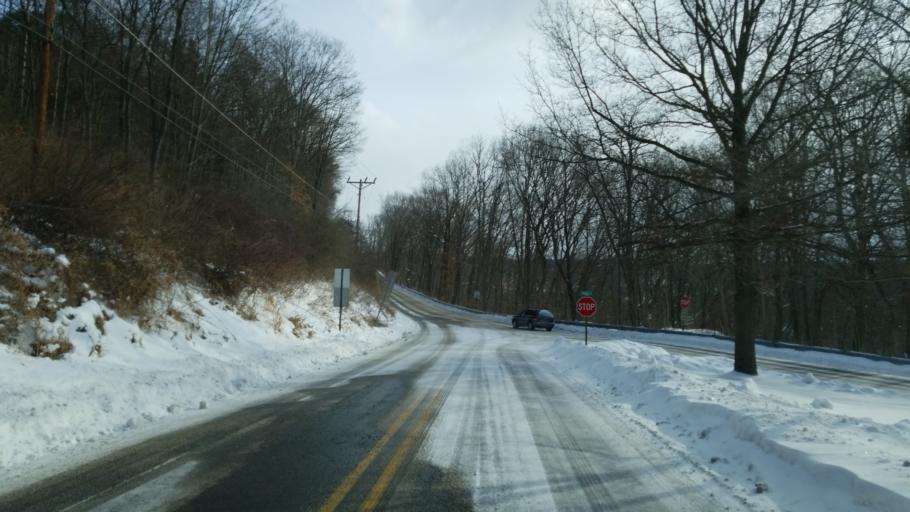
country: US
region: Pennsylvania
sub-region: Clearfield County
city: Clearfield
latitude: 41.0157
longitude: -78.4507
